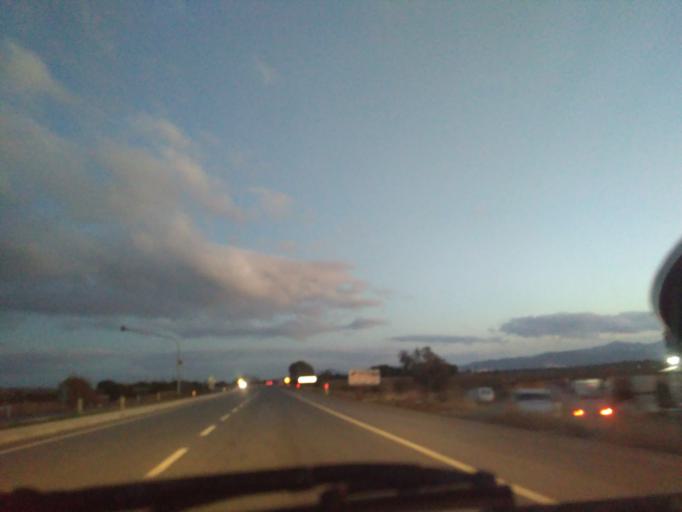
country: TR
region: Balikesir
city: Altinova
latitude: 39.1651
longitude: 26.8414
